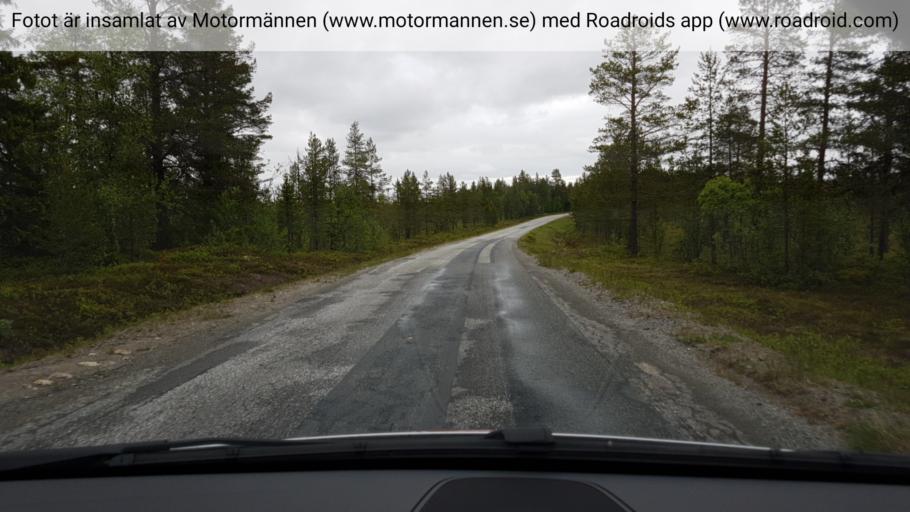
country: SE
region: Jaemtland
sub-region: Harjedalens Kommun
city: Sveg
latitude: 62.3332
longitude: 13.4256
